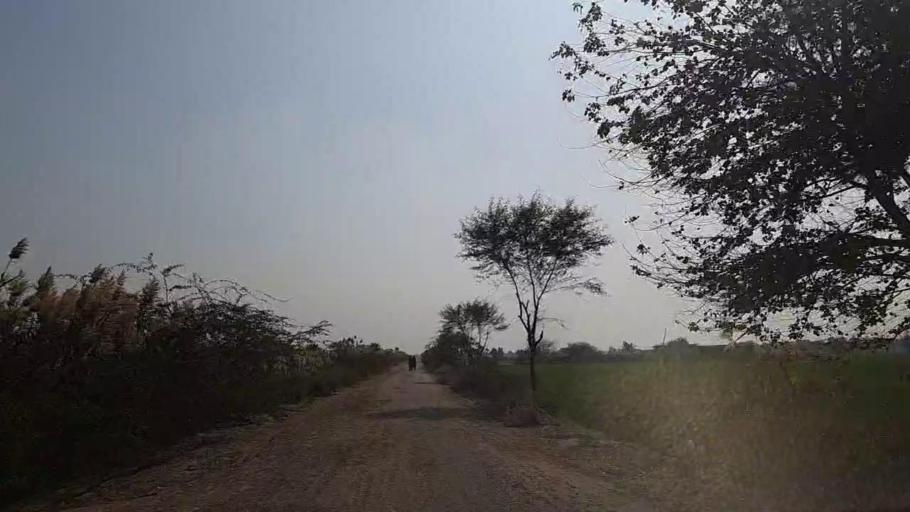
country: PK
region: Sindh
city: Daur
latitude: 26.4739
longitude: 68.4657
